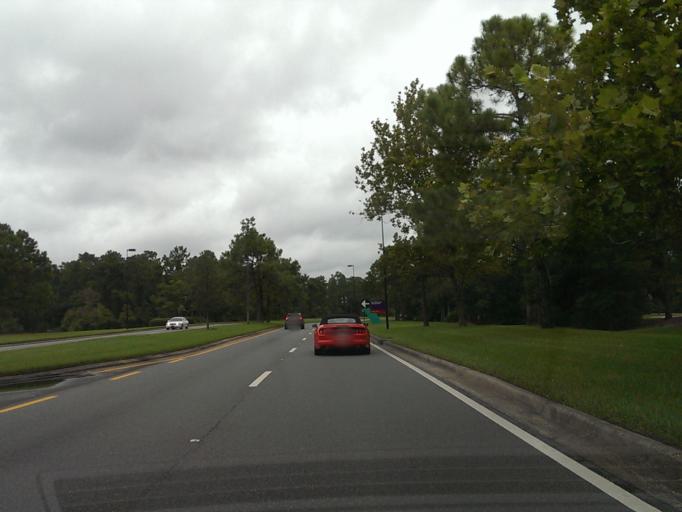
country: US
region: Florida
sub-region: Osceola County
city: Celebration
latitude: 28.3879
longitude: -81.5404
